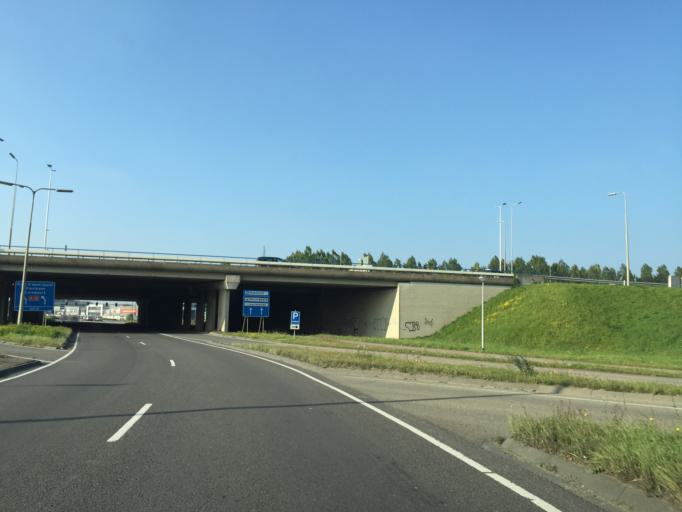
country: NL
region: South Holland
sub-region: Gemeente Barendrecht
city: Barendrecht
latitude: 51.8673
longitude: 4.5551
